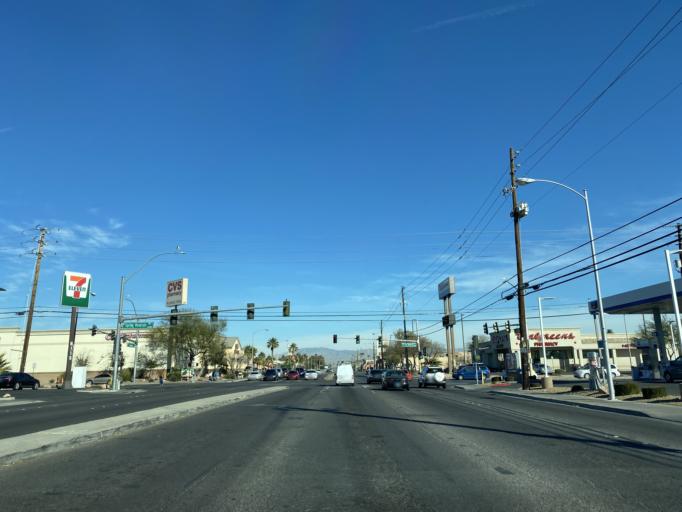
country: US
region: Nevada
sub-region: Clark County
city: Spring Valley
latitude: 36.1249
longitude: -115.2249
